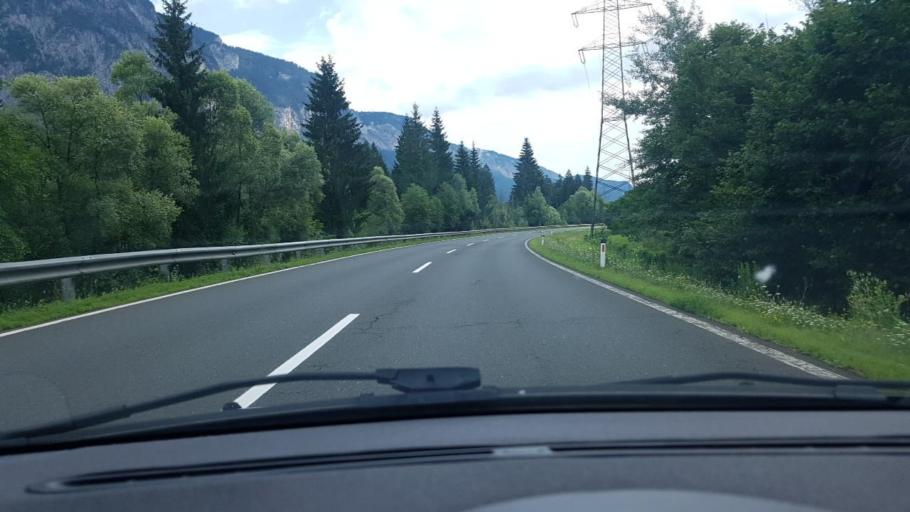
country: AT
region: Carinthia
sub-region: Politischer Bezirk Villach Land
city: Hohenthurn
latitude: 46.5682
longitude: 13.6737
